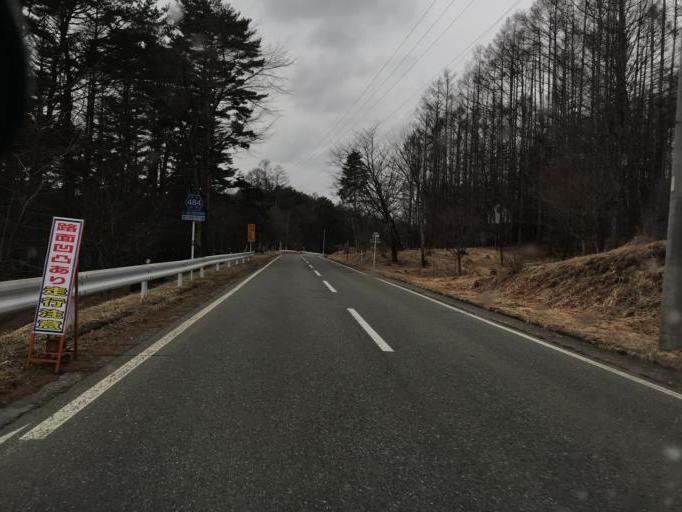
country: JP
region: Nagano
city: Chino
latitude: 35.8989
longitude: 138.3202
